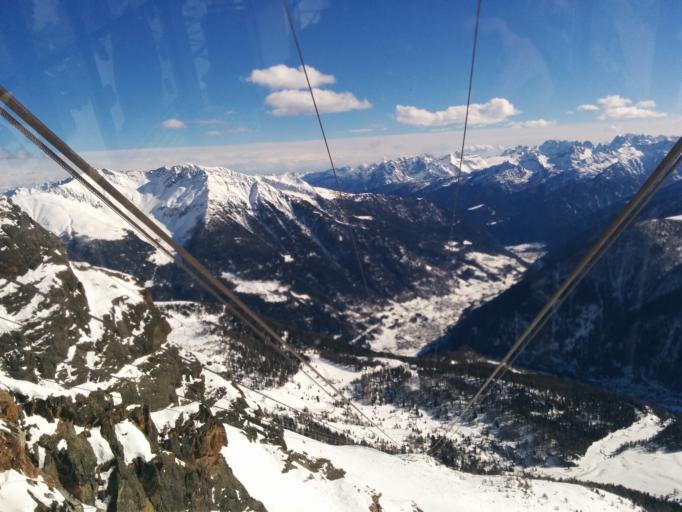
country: IT
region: Trentino-Alto Adige
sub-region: Provincia di Trento
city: Cogolo
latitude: 46.3805
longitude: 10.6375
